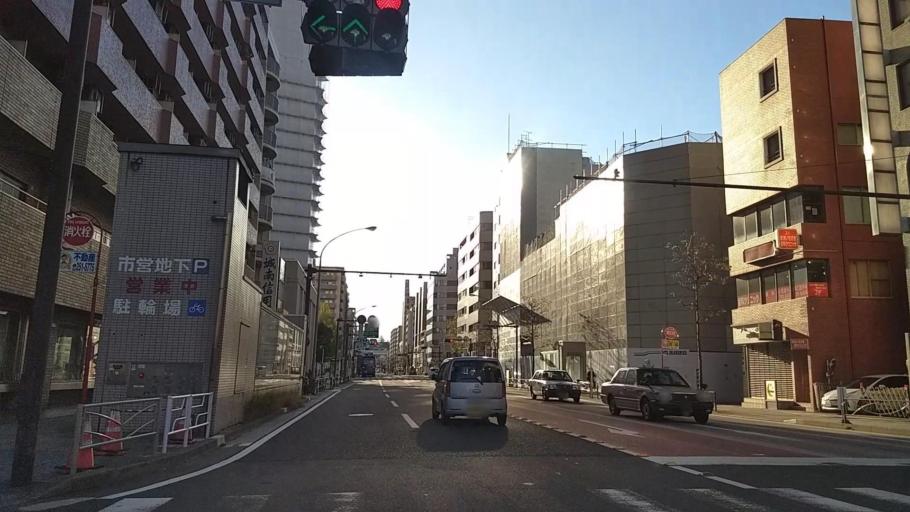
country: JP
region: Kanagawa
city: Yokohama
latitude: 35.4422
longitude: 139.6316
